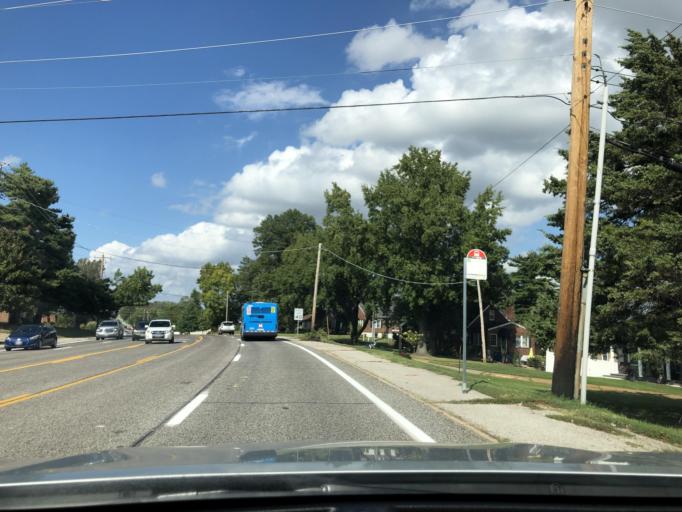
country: US
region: Missouri
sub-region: Saint Louis County
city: Lakeshire
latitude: 38.5403
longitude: -90.3334
